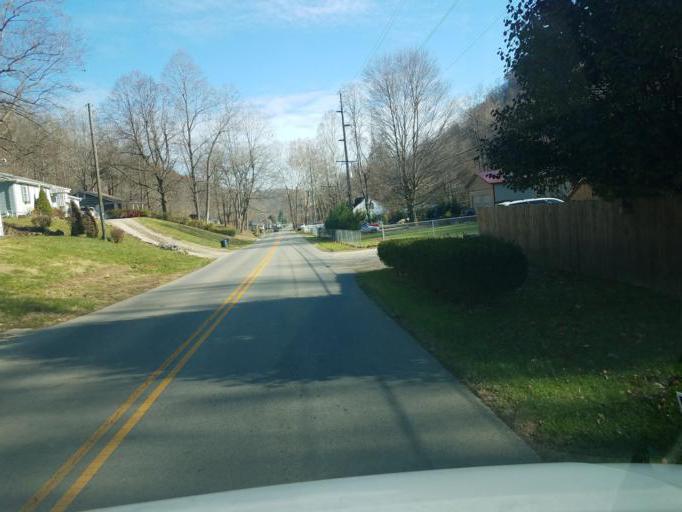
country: US
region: Ohio
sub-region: Scioto County
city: New Boston
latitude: 38.7631
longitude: -82.9500
